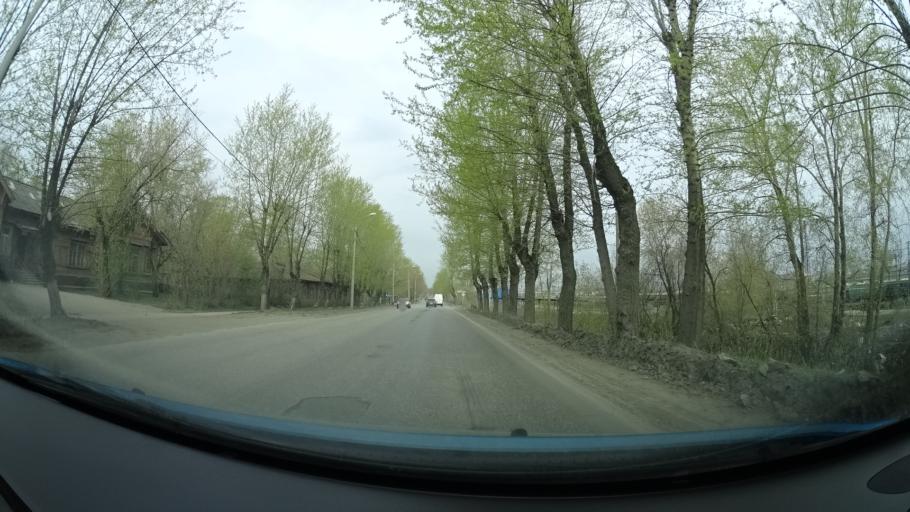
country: RU
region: Perm
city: Perm
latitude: 58.0021
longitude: 56.1779
